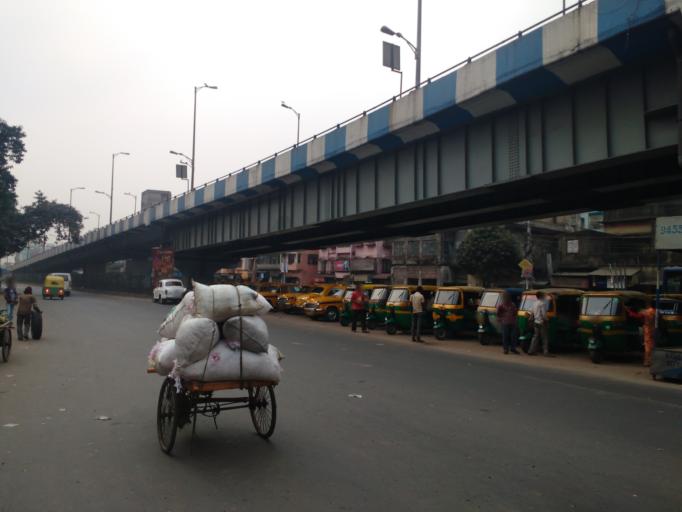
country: IN
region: West Bengal
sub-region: North 24 Parganas
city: Baranagar
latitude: 22.6524
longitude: 88.3768
